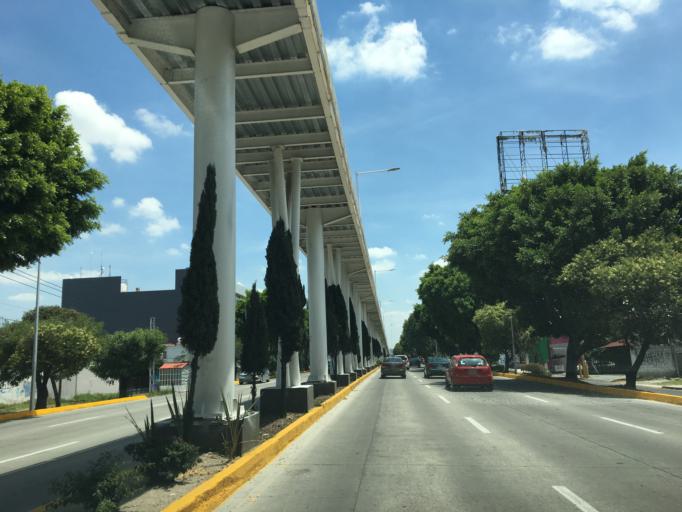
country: MX
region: Puebla
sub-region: Cuautlancingo
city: Sanctorum
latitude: 19.0835
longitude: -98.2286
